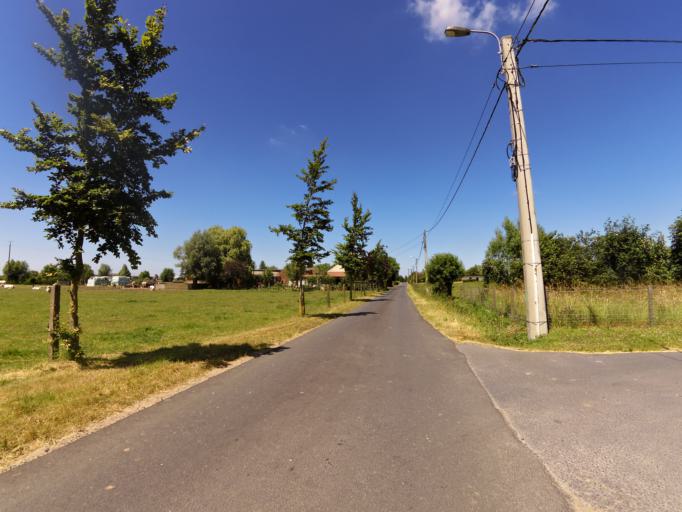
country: BE
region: Flanders
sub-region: Provincie West-Vlaanderen
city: Torhout
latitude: 51.0992
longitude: 3.0685
